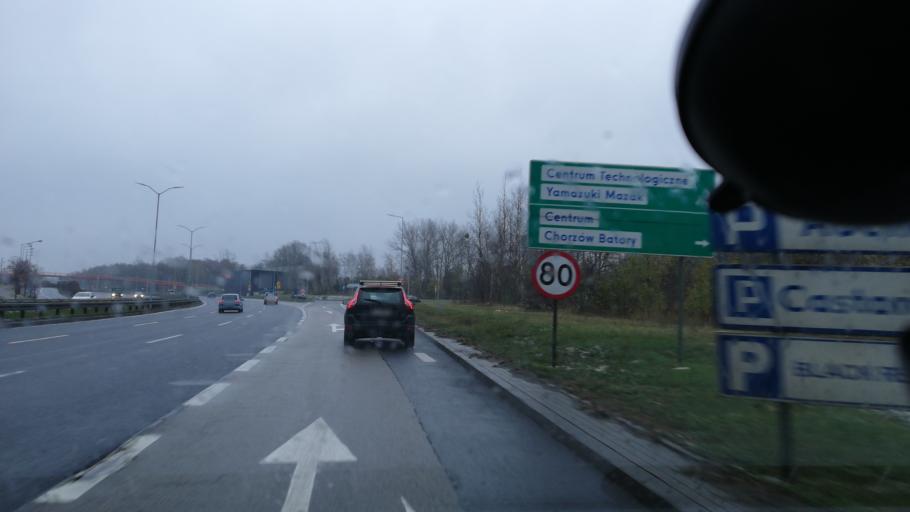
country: PL
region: Silesian Voivodeship
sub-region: Chorzow
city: Chorzow
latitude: 50.2746
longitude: 18.9612
